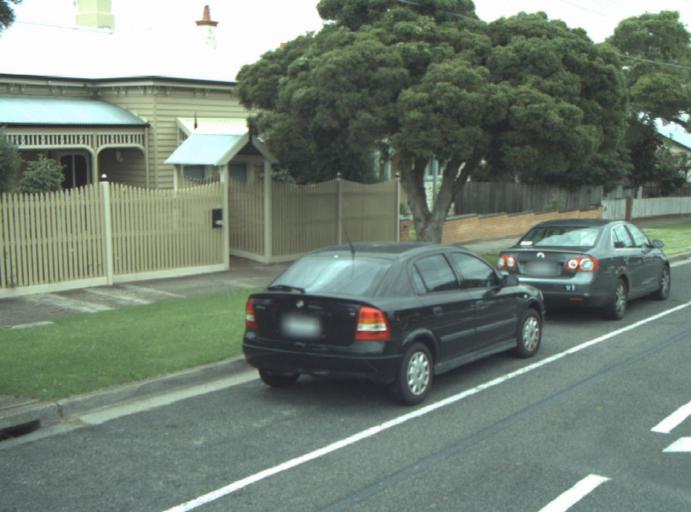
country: AU
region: Victoria
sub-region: Greater Geelong
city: East Geelong
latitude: -38.1567
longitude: 144.3650
